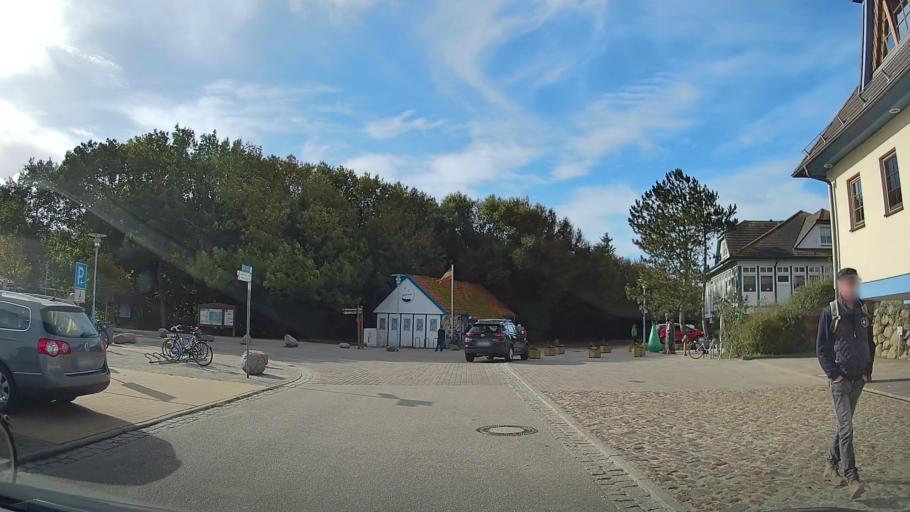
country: DE
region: Mecklenburg-Vorpommern
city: Ostseebad Dierhagen
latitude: 54.3519
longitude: 12.3877
